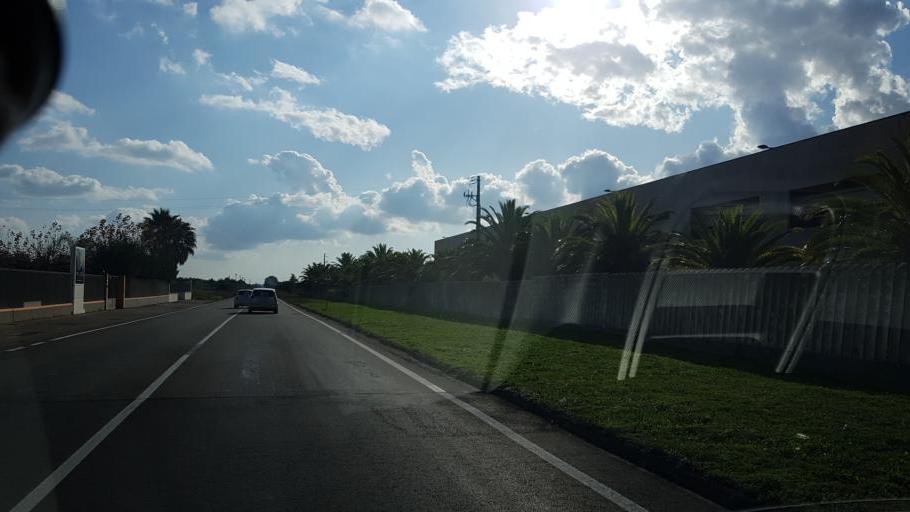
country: IT
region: Apulia
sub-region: Provincia di Lecce
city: Salice Salentino
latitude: 40.3669
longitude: 17.9672
